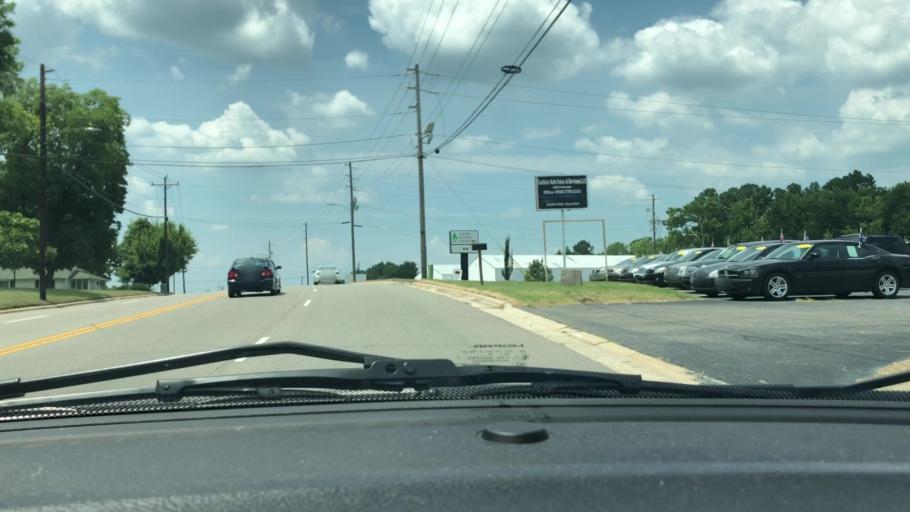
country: US
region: North Carolina
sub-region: Lee County
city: Sanford
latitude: 35.4914
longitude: -79.1902
